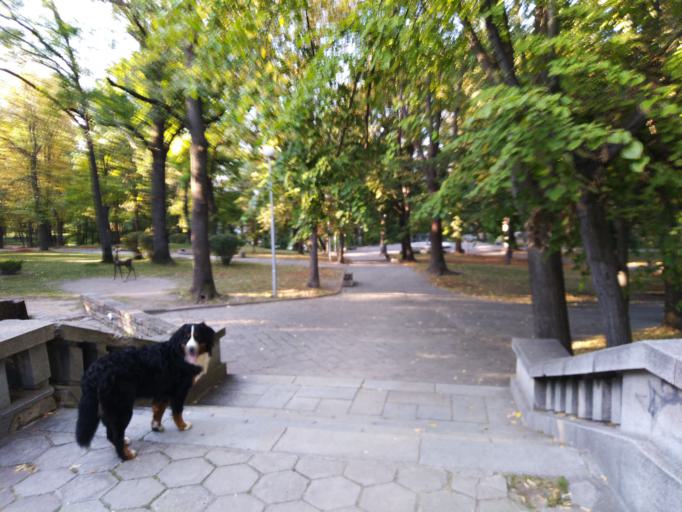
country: BG
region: Plovdiv
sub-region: Obshtina Khisarya
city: Khisarya
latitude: 42.5018
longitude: 24.7039
